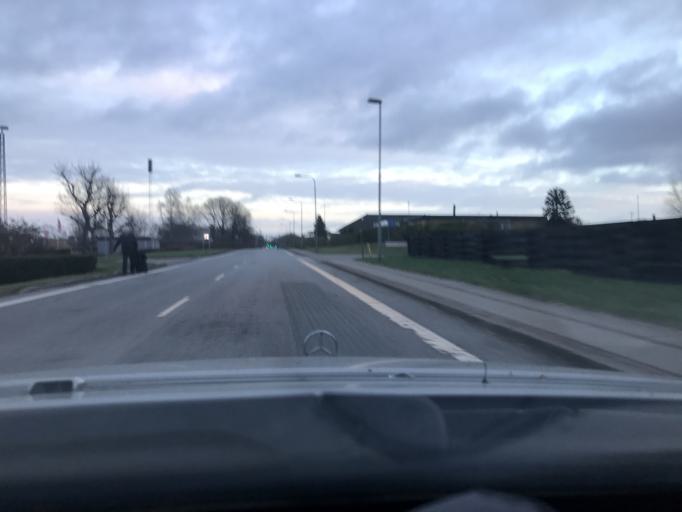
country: DK
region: South Denmark
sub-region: Sonderborg Kommune
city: Nordborg
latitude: 55.0557
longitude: 9.7389
